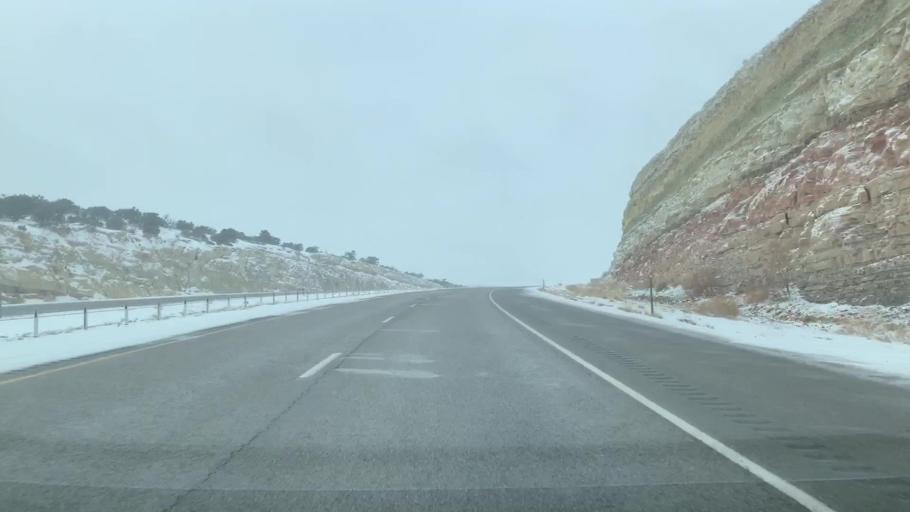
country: US
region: Utah
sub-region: Emery County
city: Ferron
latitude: 38.8494
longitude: -110.9036
